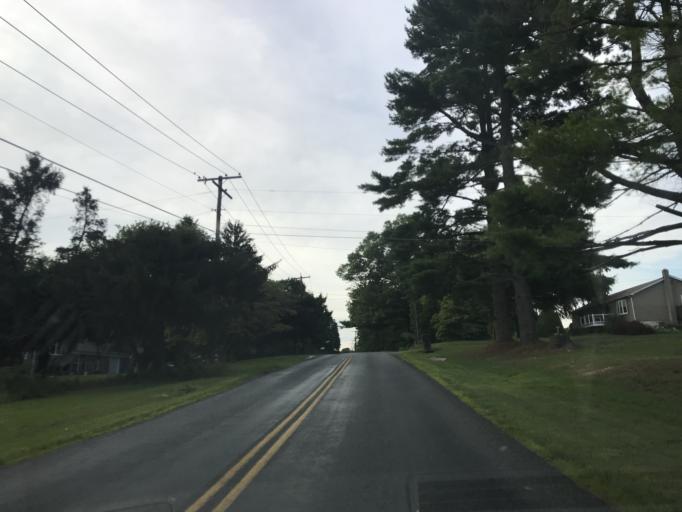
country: US
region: Maryland
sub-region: Harford County
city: Perryman
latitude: 39.5055
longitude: -76.2062
